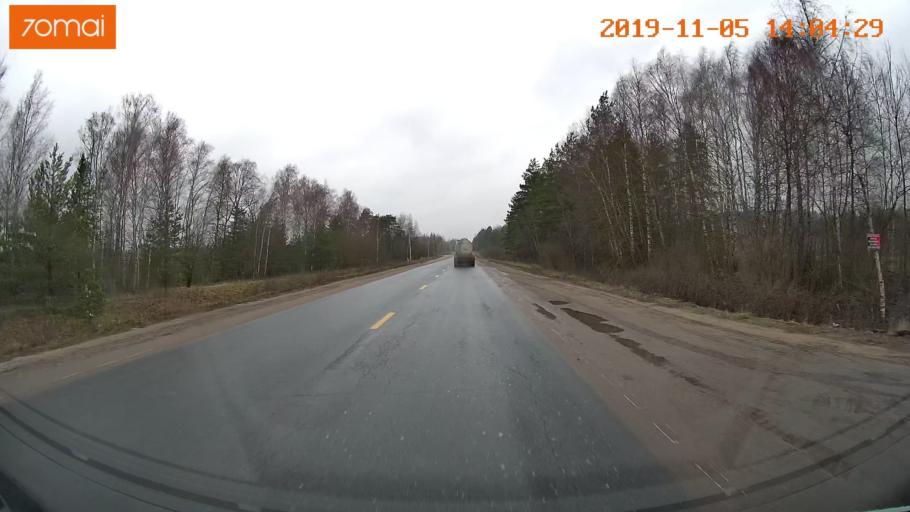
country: RU
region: Ivanovo
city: Kokhma
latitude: 56.9974
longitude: 41.1754
